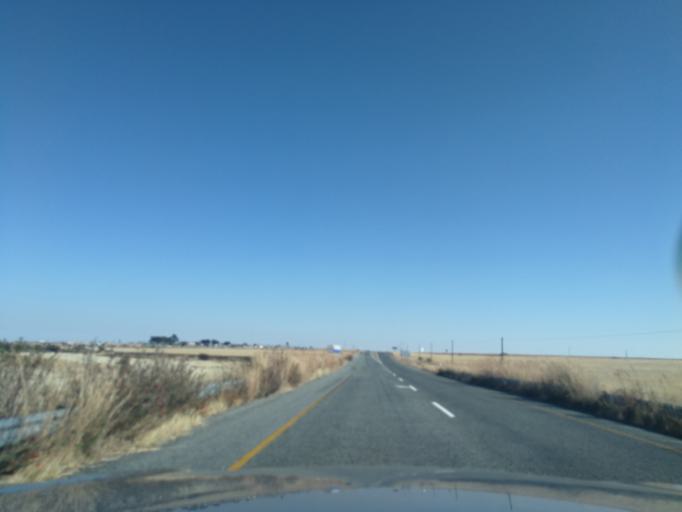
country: ZA
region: Orange Free State
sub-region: Thabo Mofutsanyana District Municipality
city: Senekal
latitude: -27.9430
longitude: 27.5657
